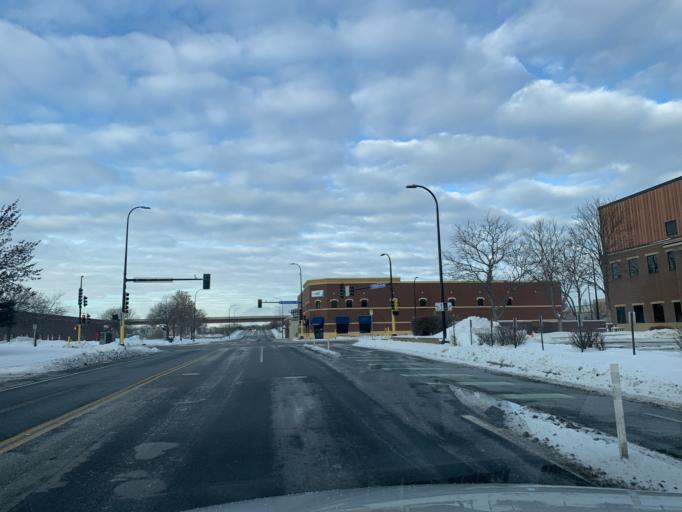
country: US
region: Minnesota
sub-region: Hennepin County
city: Minneapolis
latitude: 44.9921
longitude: -93.2806
